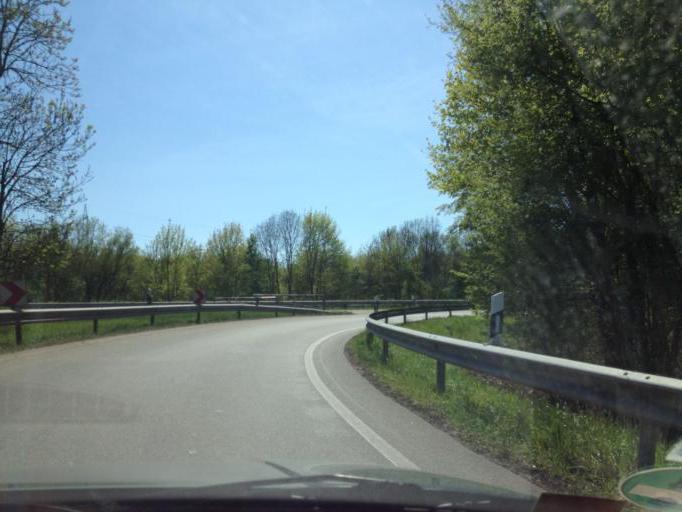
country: DE
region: Rheinland-Pfalz
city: Neuhofen
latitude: 49.4352
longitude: 8.4092
